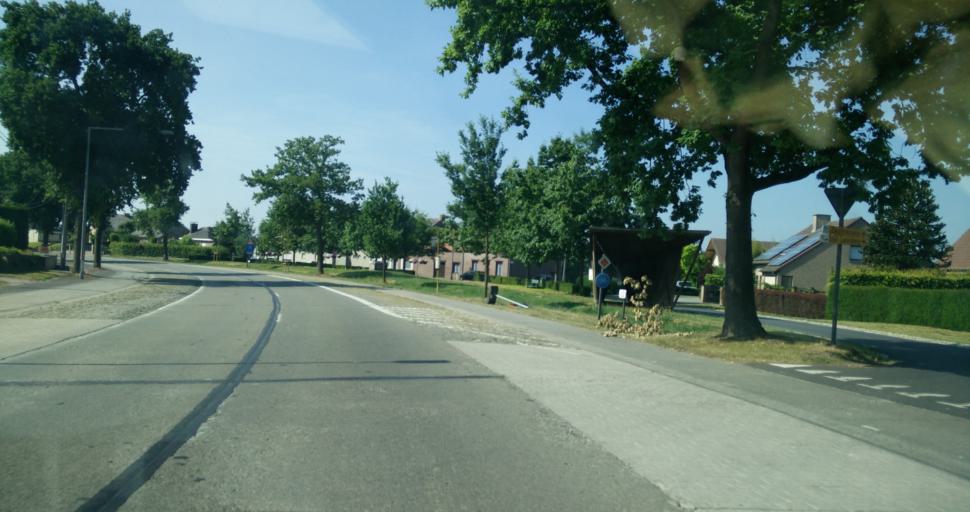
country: BE
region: Flanders
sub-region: Provincie Oost-Vlaanderen
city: Zottegem
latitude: 50.8866
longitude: 3.7332
